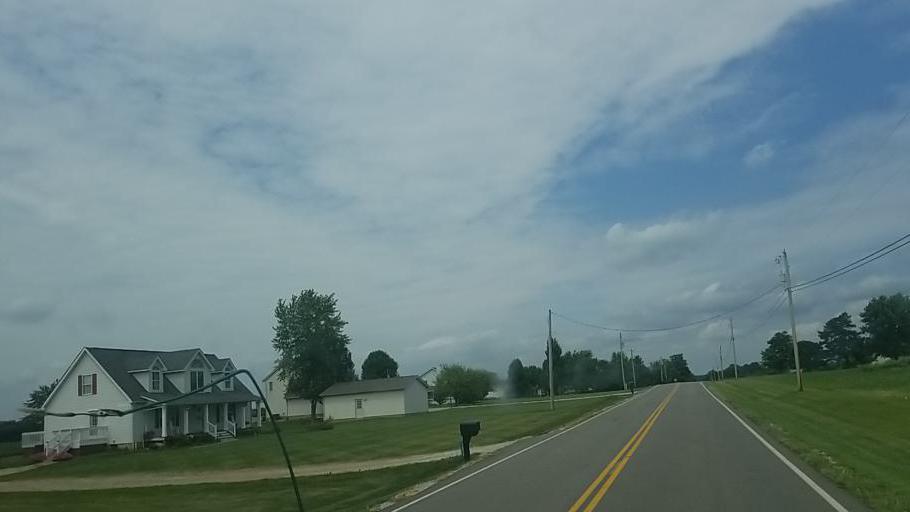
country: US
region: Ohio
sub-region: Pickaway County
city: Ashville
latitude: 39.7559
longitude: -82.9128
